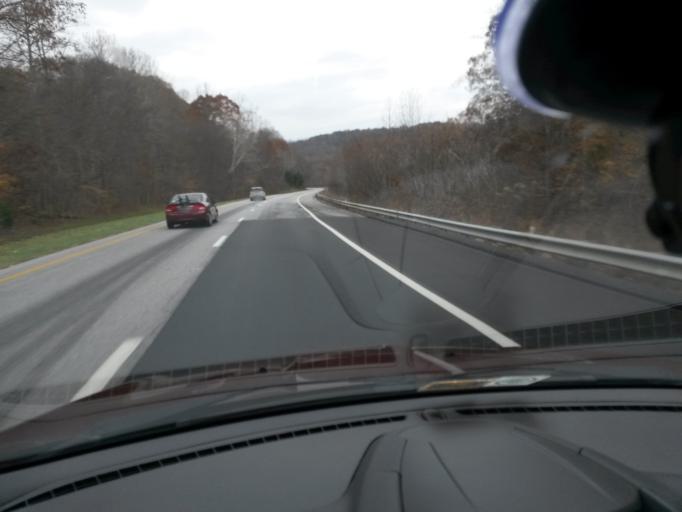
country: US
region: Virginia
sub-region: Nelson County
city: Nellysford
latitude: 37.8562
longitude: -78.7451
